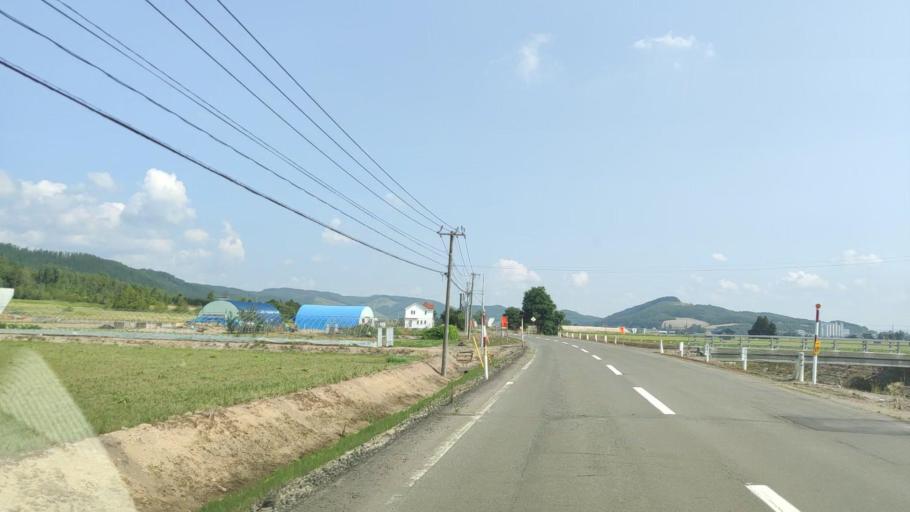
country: JP
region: Hokkaido
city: Shimo-furano
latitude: 43.3828
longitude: 142.3921
